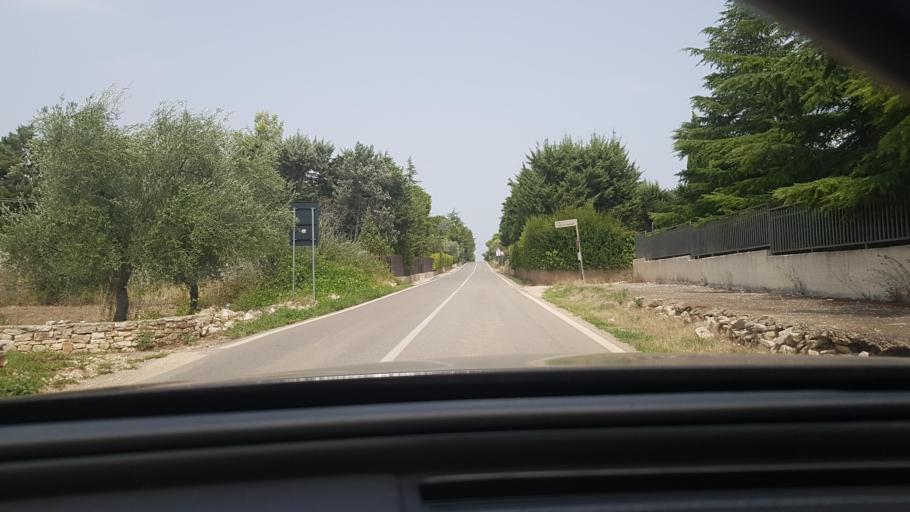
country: IT
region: Apulia
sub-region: Provincia di Barletta - Andria - Trani
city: Andria
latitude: 41.1198
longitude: 16.2846
